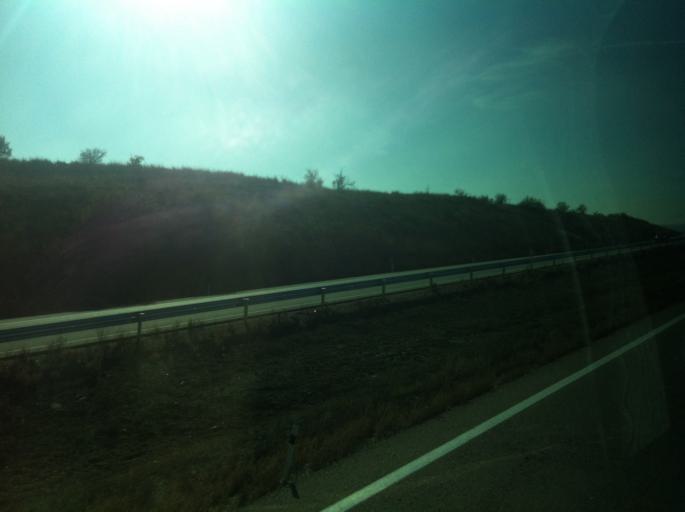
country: ES
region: Castille and Leon
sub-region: Provincia de Burgos
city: Cardenajimeno
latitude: 42.3572
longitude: -3.5990
